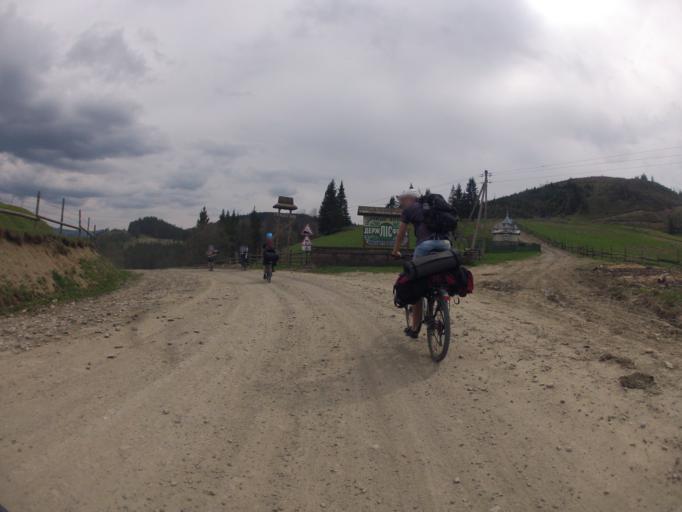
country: UA
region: Chernivtsi
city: Putyla
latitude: 47.8888
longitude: 25.1651
